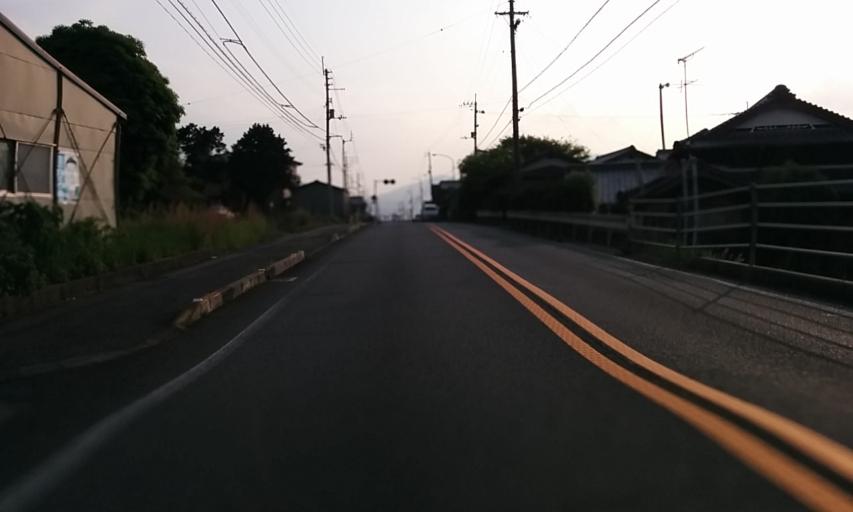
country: JP
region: Ehime
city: Saijo
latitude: 33.8804
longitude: 133.0733
